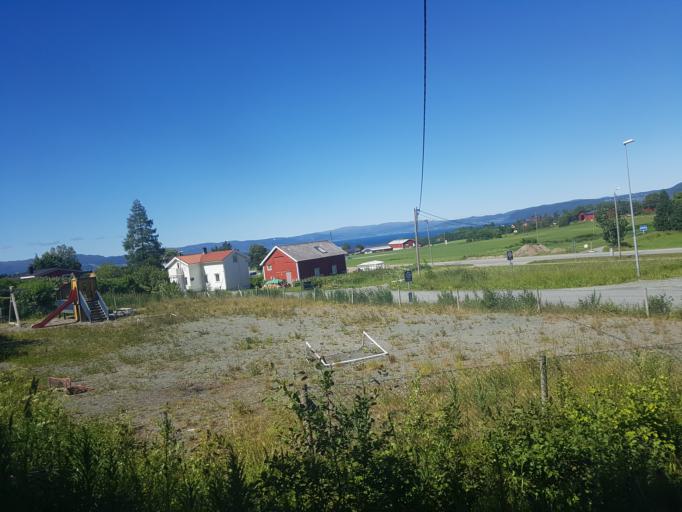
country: NO
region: Sor-Trondelag
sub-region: Skaun
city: Borsa
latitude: 63.4450
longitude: 10.1986
